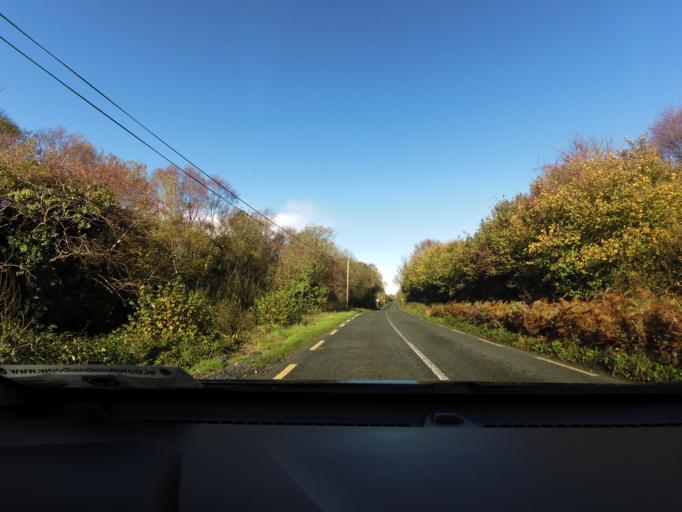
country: IE
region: Connaught
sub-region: Maigh Eo
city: Ballinrobe
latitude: 53.7004
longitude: -9.2930
